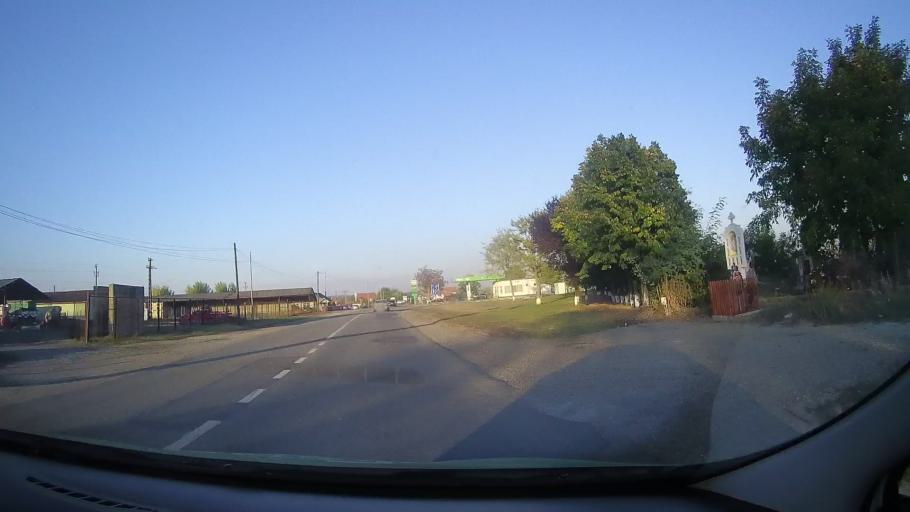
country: RO
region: Bihor
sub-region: Comuna Salard
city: Salard
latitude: 47.2105
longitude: 22.0217
